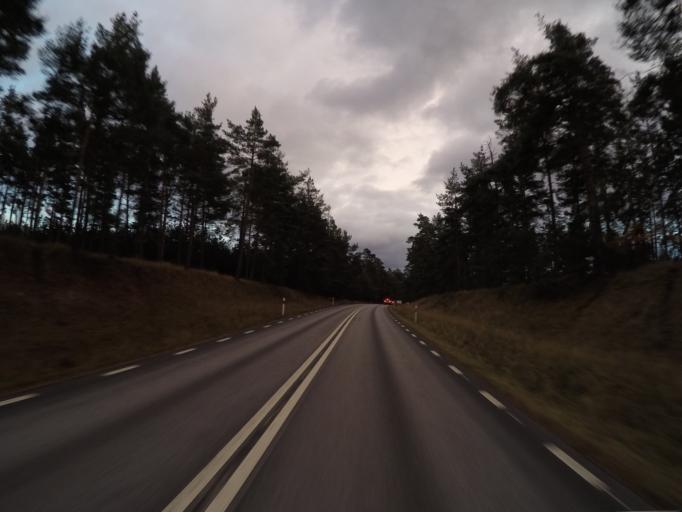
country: SE
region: Skane
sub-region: Kristianstads Kommun
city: Degeberga
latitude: 55.8757
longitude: 14.0885
